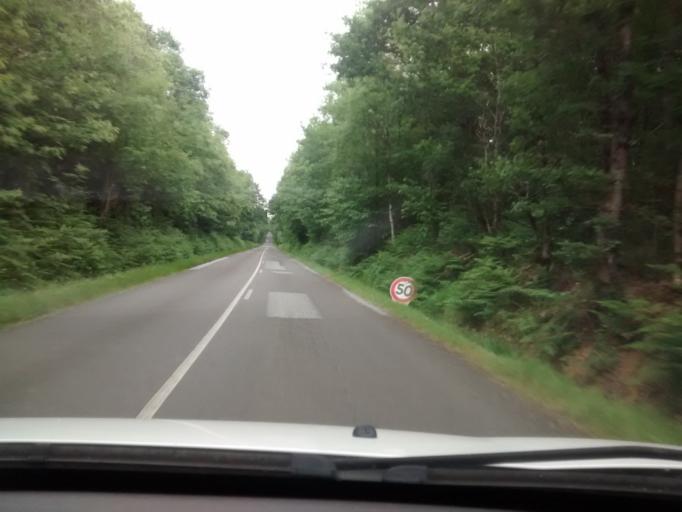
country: FR
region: Brittany
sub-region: Departement d'Ille-et-Vilaine
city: Servon-sur-Vilaine
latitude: 48.1447
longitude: -1.4470
